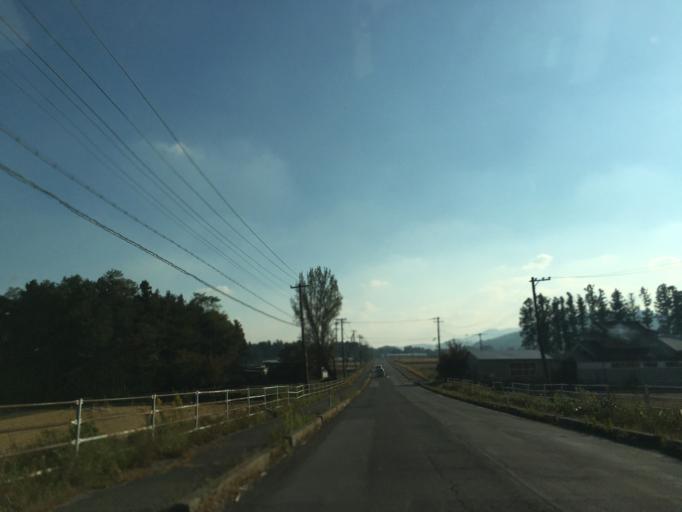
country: JP
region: Fukushima
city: Koriyama
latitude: 37.4059
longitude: 140.2704
